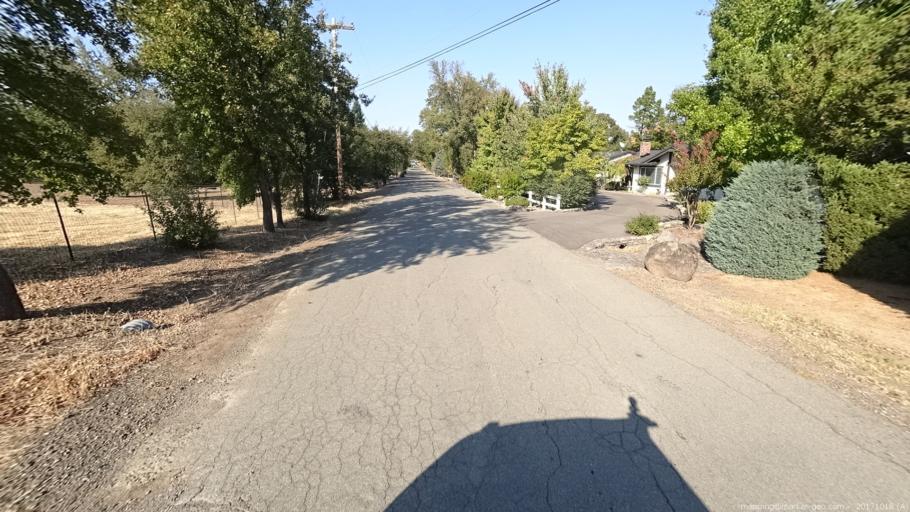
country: US
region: California
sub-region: Shasta County
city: Palo Cedro
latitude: 40.5726
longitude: -122.2321
